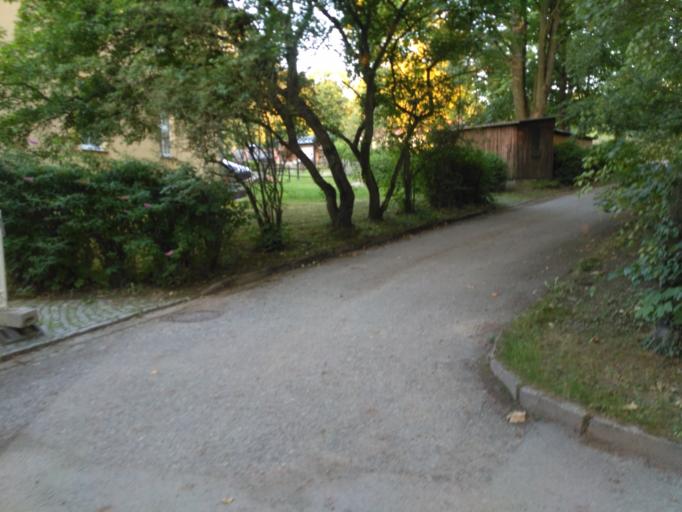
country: DE
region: Saxony
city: Demitz-Thumitz
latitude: 51.1238
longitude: 14.2376
